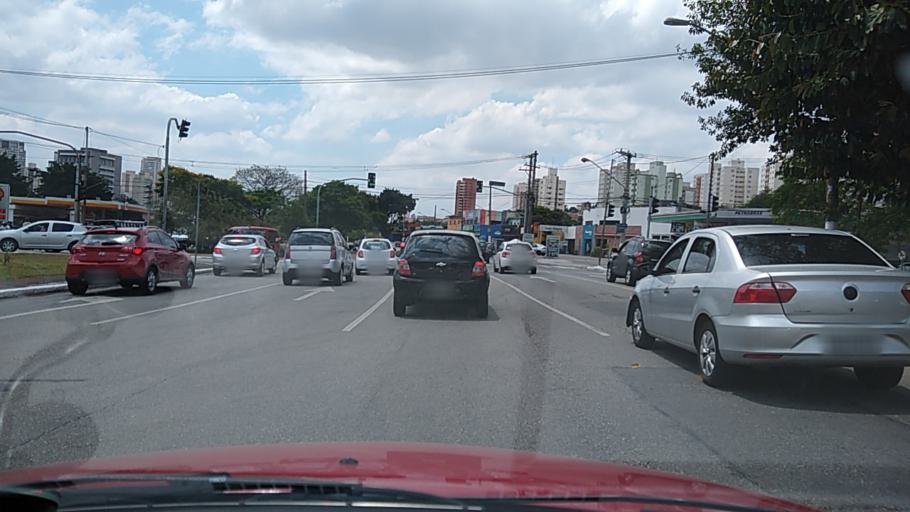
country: BR
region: Sao Paulo
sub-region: Sao Paulo
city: Sao Paulo
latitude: -23.6160
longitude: -46.6271
